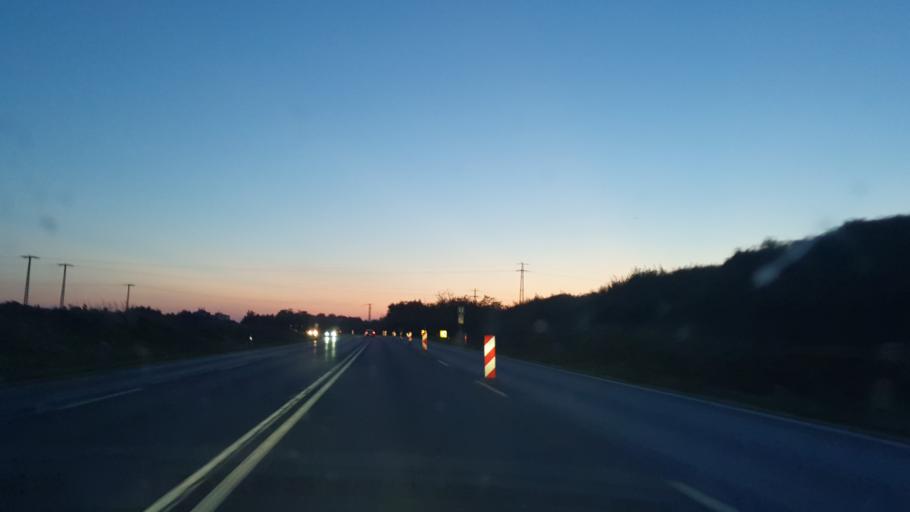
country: HU
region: Veszprem
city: Veszprem
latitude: 47.0991
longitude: 17.9418
